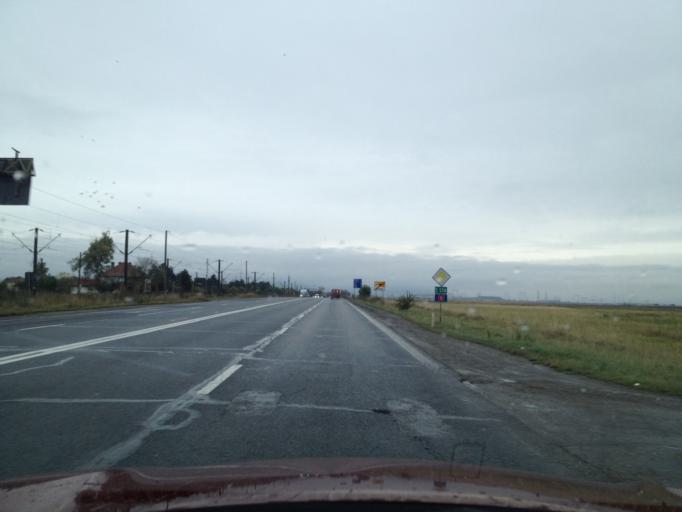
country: RO
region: Brasov
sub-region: Comuna Harman
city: Harman
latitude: 45.7000
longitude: 25.6888
